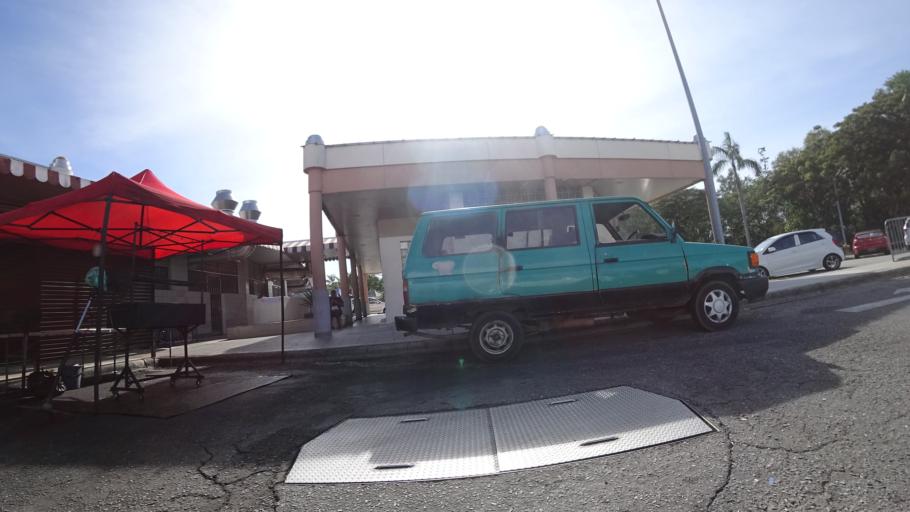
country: BN
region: Brunei and Muara
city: Bandar Seri Begawan
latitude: 4.9375
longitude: 114.8335
